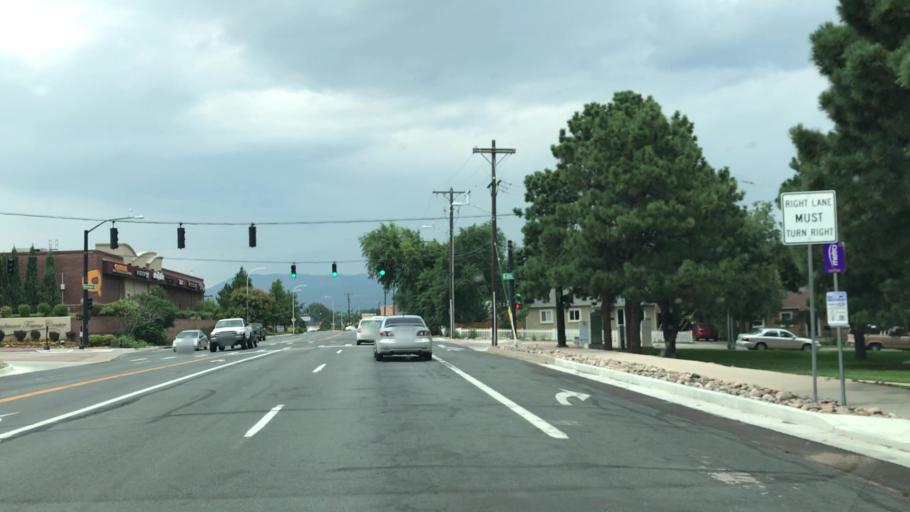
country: US
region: Colorado
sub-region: El Paso County
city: Colorado Springs
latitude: 38.8041
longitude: -104.8188
